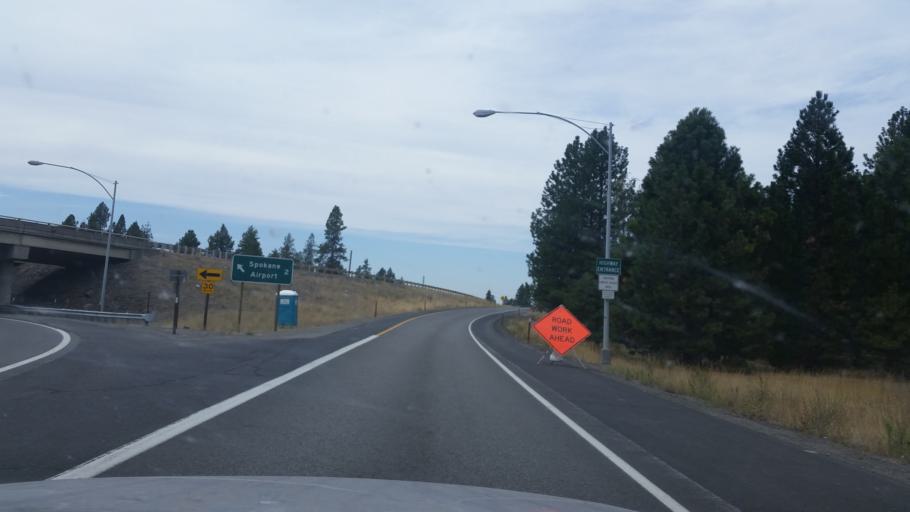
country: US
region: Washington
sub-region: Spokane County
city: Spokane
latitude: 47.6430
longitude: -117.4999
